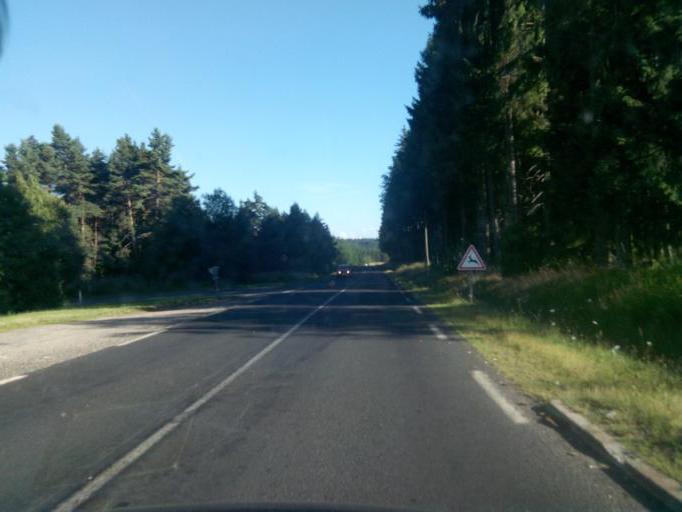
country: FR
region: Auvergne
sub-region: Departement de la Haute-Loire
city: Fontannes
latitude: 45.3090
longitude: 3.6989
